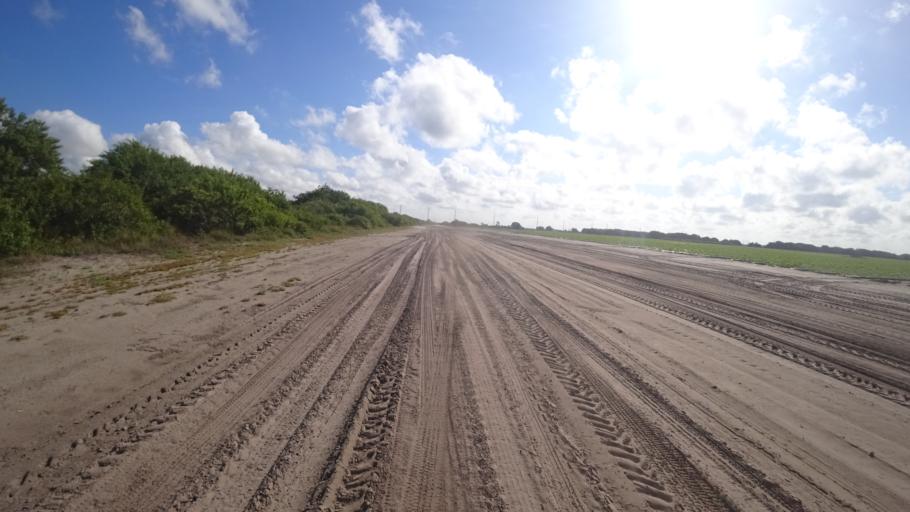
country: US
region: Florida
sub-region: Manatee County
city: Ellenton
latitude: 27.5130
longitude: -82.3286
